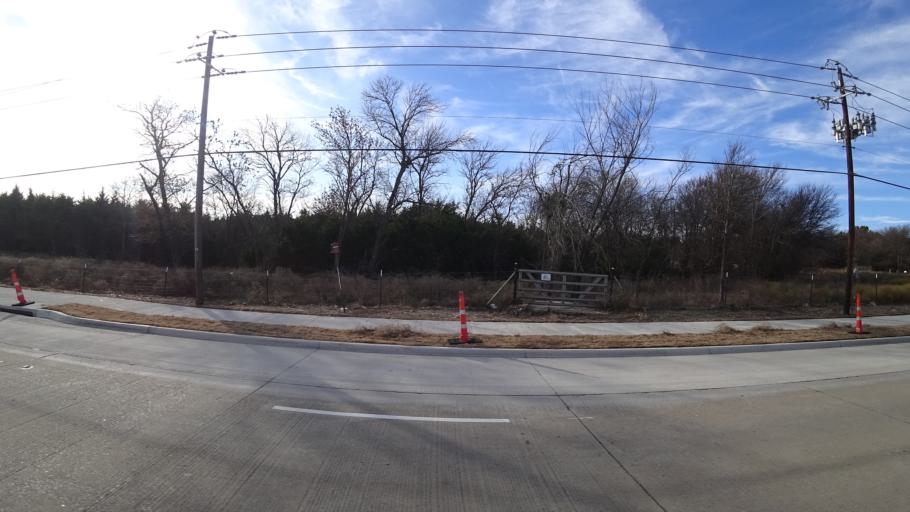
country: US
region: Texas
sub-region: Collin County
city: McKinney
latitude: 33.1966
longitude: -96.6683
